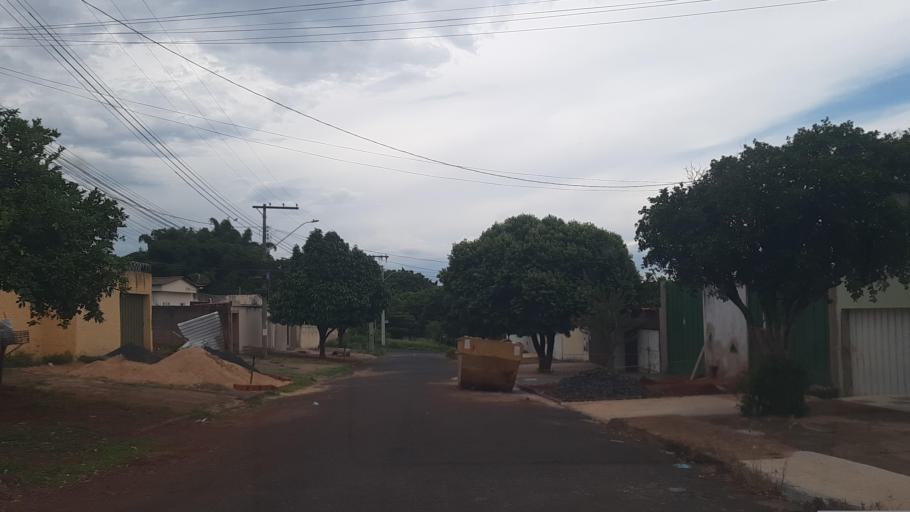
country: BR
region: Minas Gerais
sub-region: Uberlandia
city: Uberlandia
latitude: -18.9230
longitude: -48.3013
